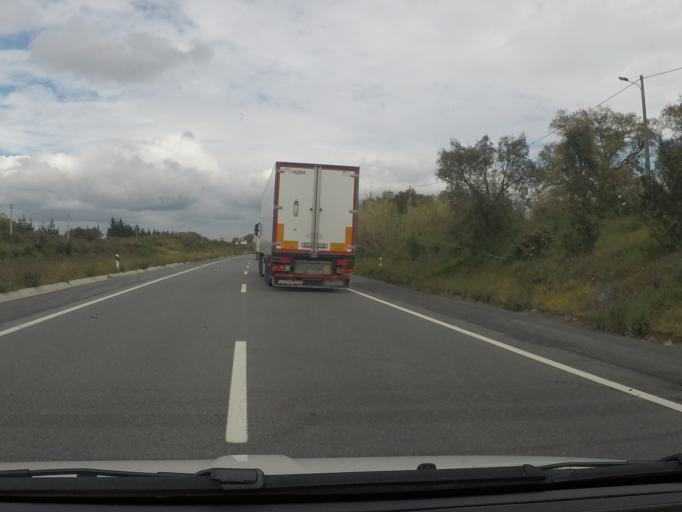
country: PT
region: Setubal
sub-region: Santiago do Cacem
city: Santiago do Cacem
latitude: 38.0707
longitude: -8.6710
